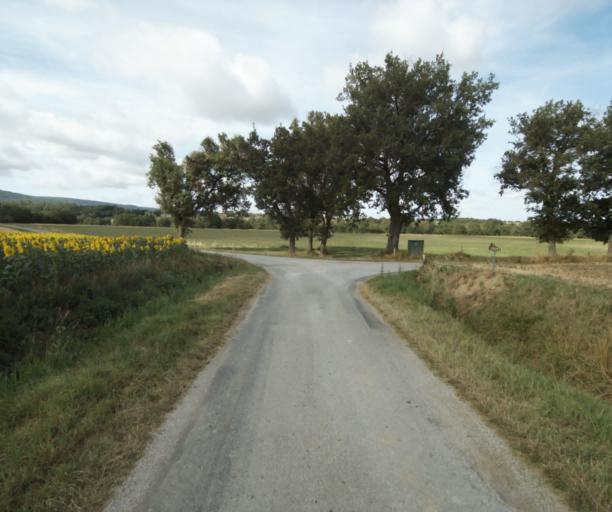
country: FR
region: Midi-Pyrenees
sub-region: Departement du Tarn
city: Soreze
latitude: 43.4761
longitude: 2.0855
